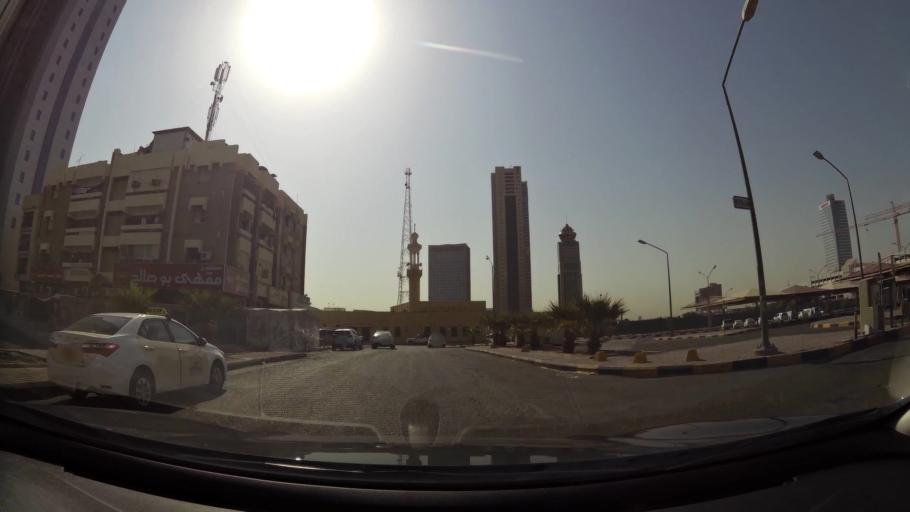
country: KW
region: Al Asimah
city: Kuwait City
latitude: 29.3676
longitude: 47.9790
